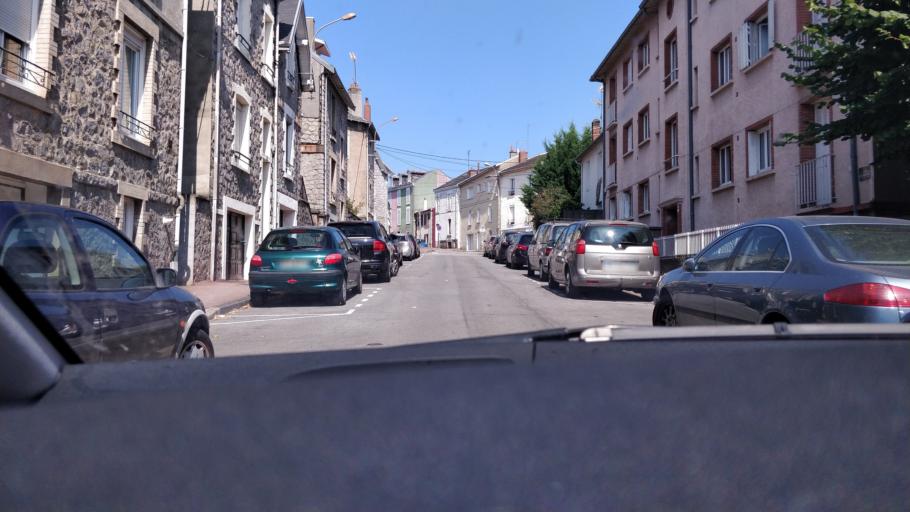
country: FR
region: Limousin
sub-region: Departement de la Haute-Vienne
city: Limoges
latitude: 45.8397
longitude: 1.2685
